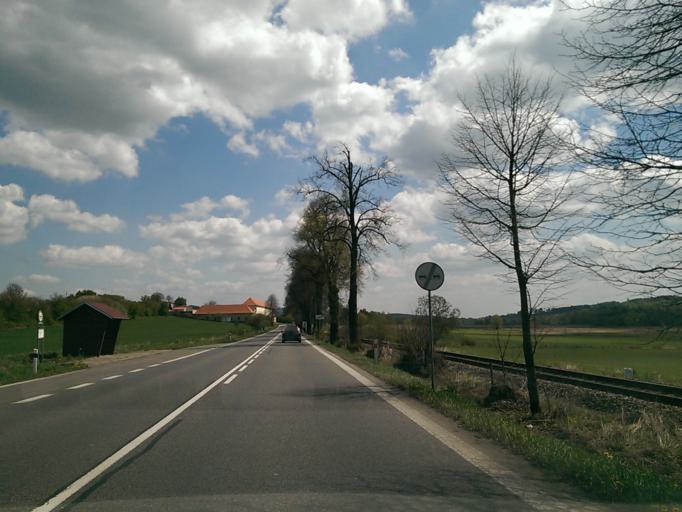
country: CZ
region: Liberecky
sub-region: Okres Semily
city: Turnov
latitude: 50.5720
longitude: 15.1744
